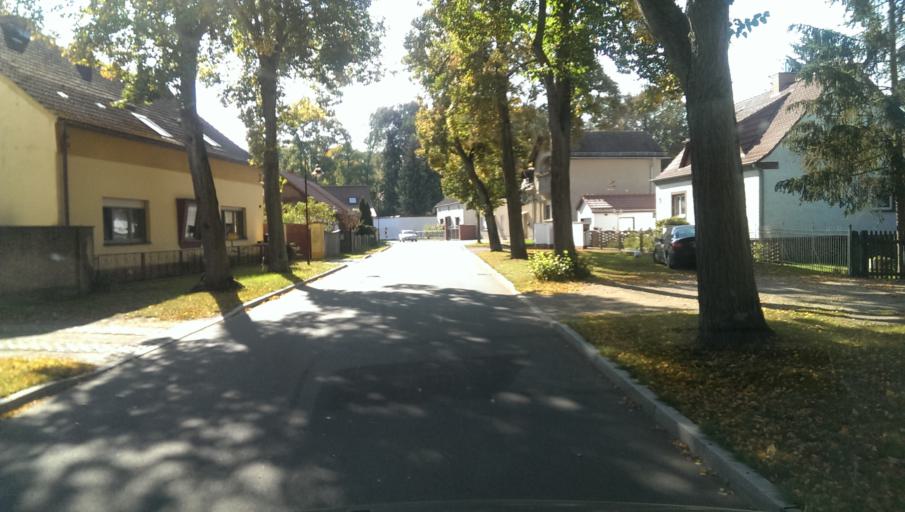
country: DE
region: Brandenburg
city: Halbe
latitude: 52.0553
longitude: 13.7149
